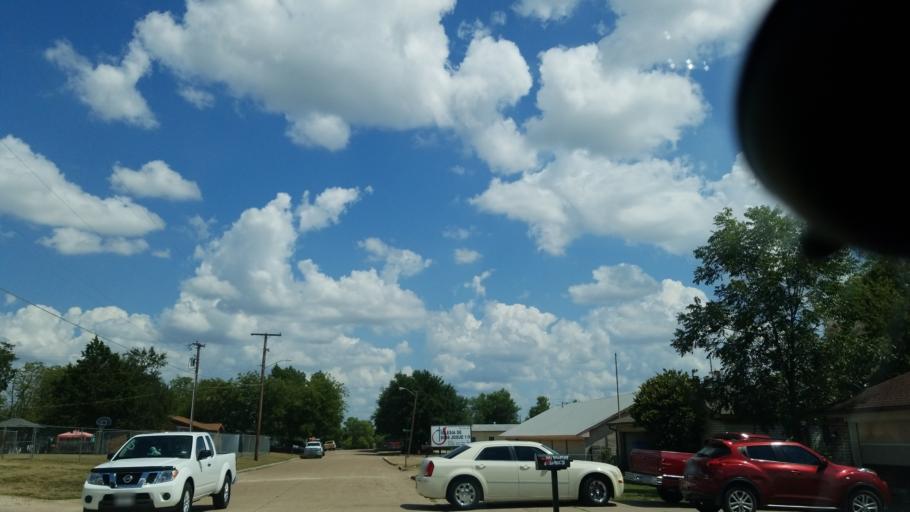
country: US
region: Texas
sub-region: Dallas County
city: Grand Prairie
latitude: 32.7285
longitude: -96.9935
